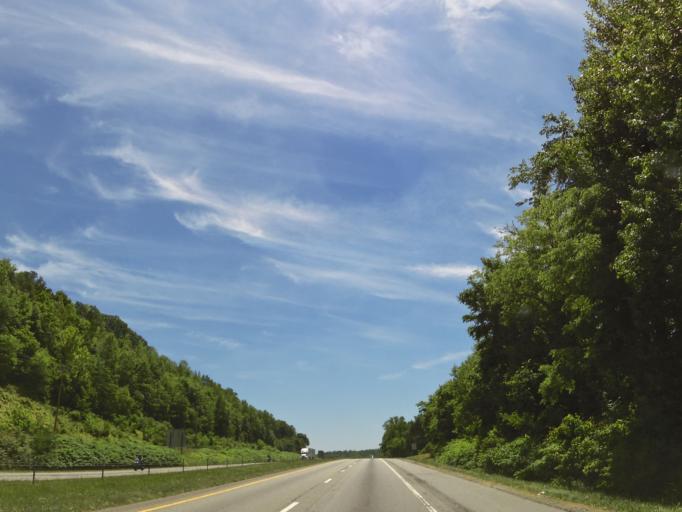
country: US
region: Tennessee
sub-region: Campbell County
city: Caryville
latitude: 36.2837
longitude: -84.2112
